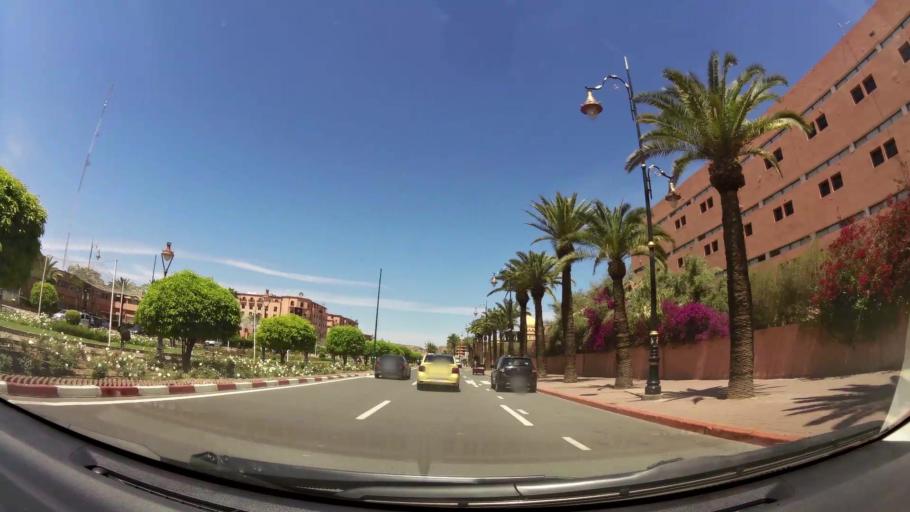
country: MA
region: Marrakech-Tensift-Al Haouz
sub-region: Marrakech
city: Marrakesh
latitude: 31.6277
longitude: -8.0144
